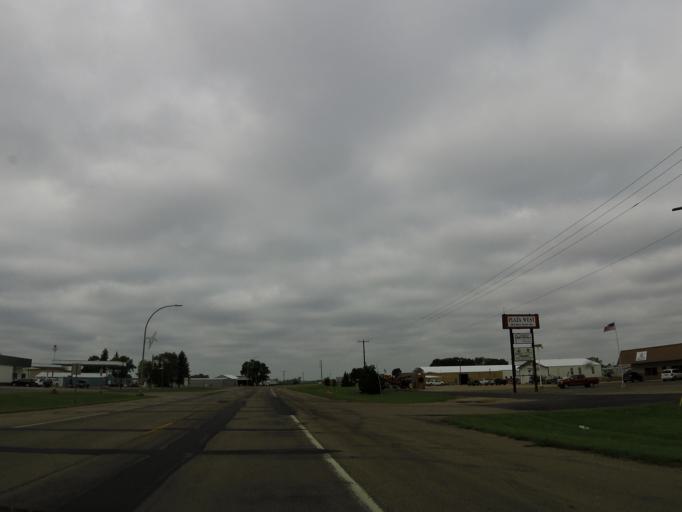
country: US
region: Minnesota
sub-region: Renville County
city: Olivia
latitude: 44.7783
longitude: -95.0236
